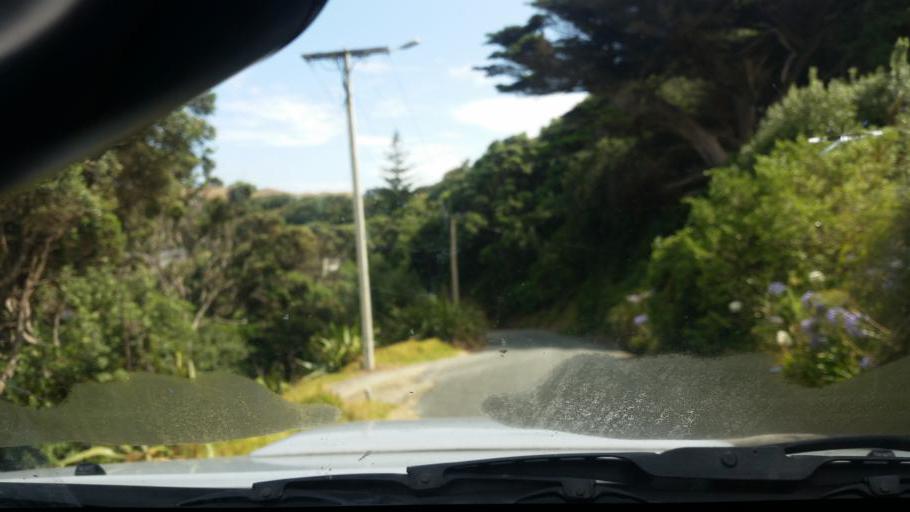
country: NZ
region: Northland
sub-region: Kaipara District
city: Dargaville
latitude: -35.9513
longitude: 173.7450
